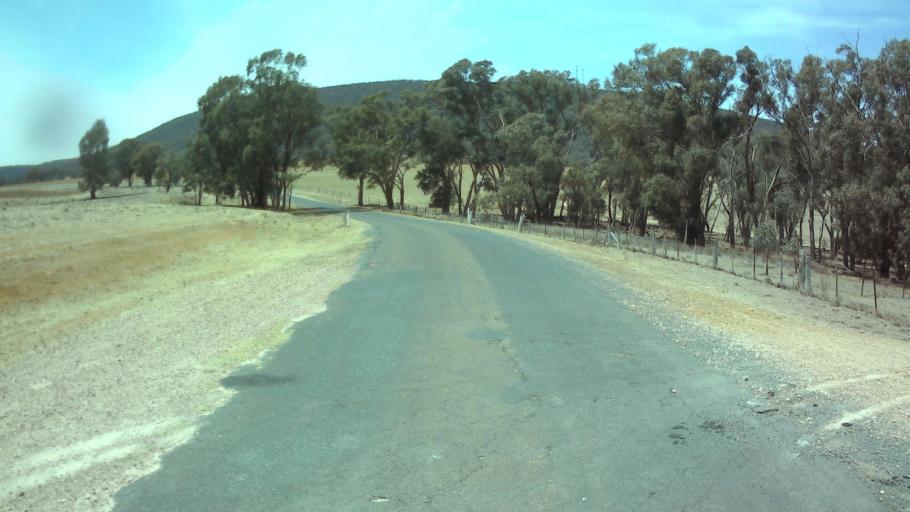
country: AU
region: New South Wales
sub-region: Weddin
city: Grenfell
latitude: -34.0346
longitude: 148.4345
